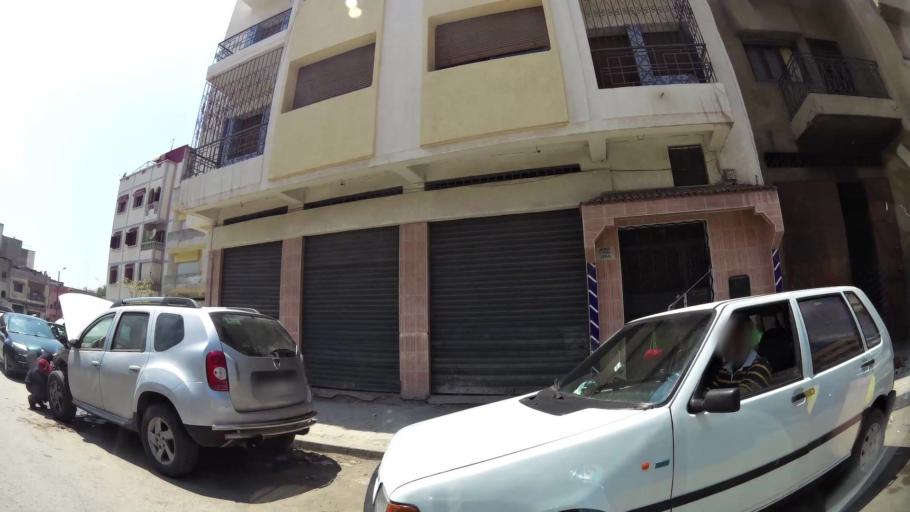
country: MA
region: Rabat-Sale-Zemmour-Zaer
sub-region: Skhirate-Temara
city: Temara
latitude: 33.9702
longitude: -6.8890
